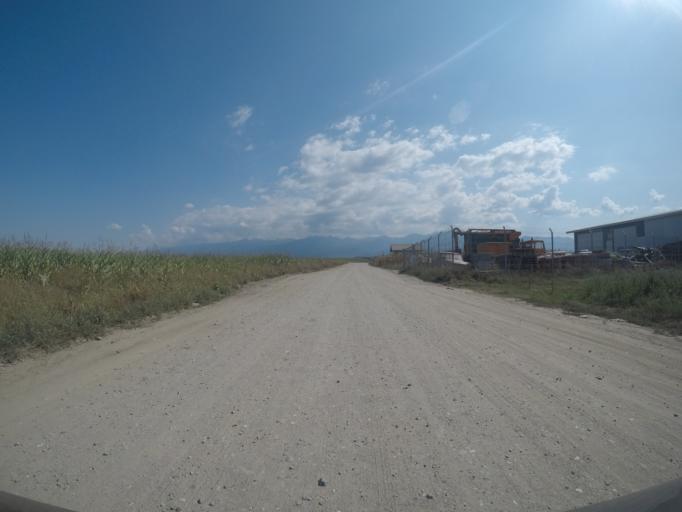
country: RO
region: Sibiu
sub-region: Comuna Avrig
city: Avrig
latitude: 45.7341
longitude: 24.3879
